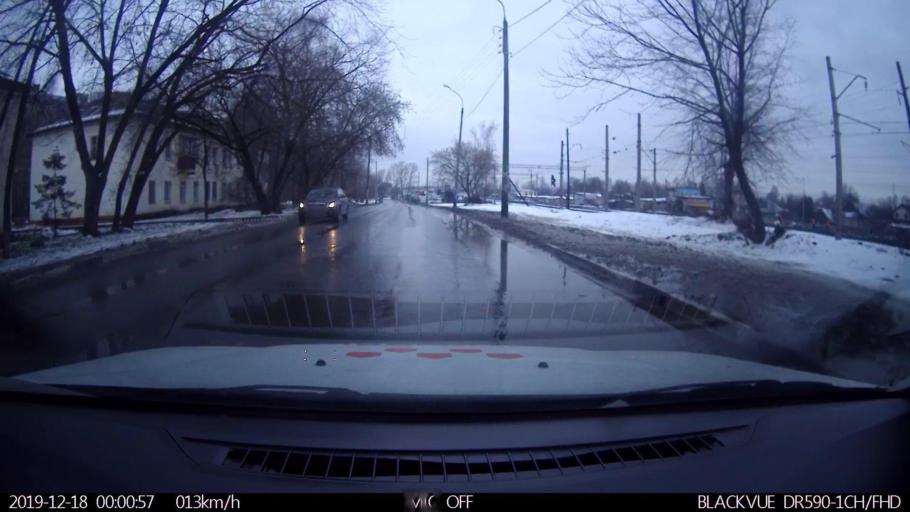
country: RU
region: Nizjnij Novgorod
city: Gorbatovka
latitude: 56.3680
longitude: 43.8271
